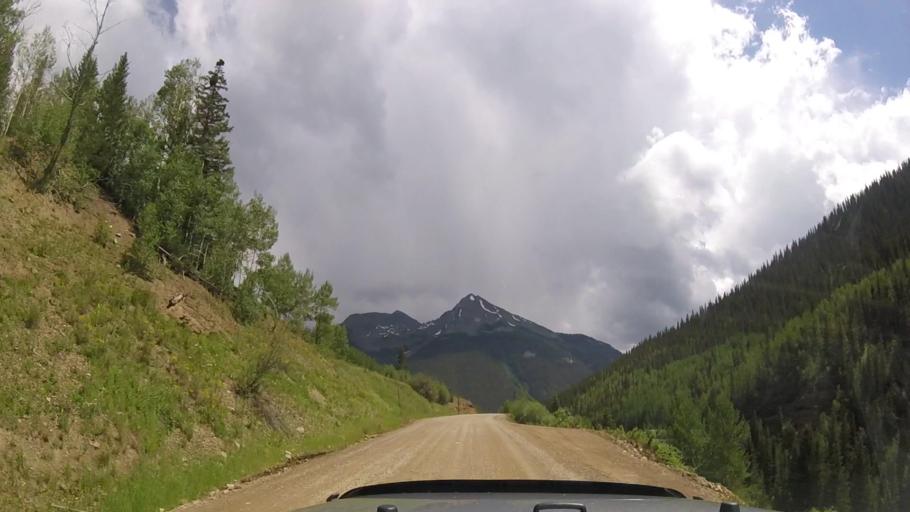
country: US
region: Colorado
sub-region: San Juan County
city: Silverton
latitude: 37.8241
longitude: -107.6662
